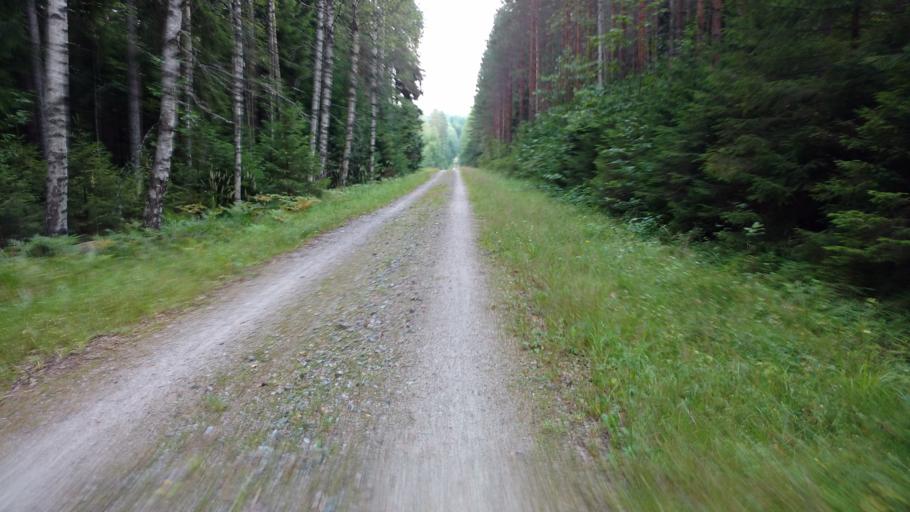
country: FI
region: Varsinais-Suomi
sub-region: Salo
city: Pertteli
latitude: 60.3963
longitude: 23.2219
